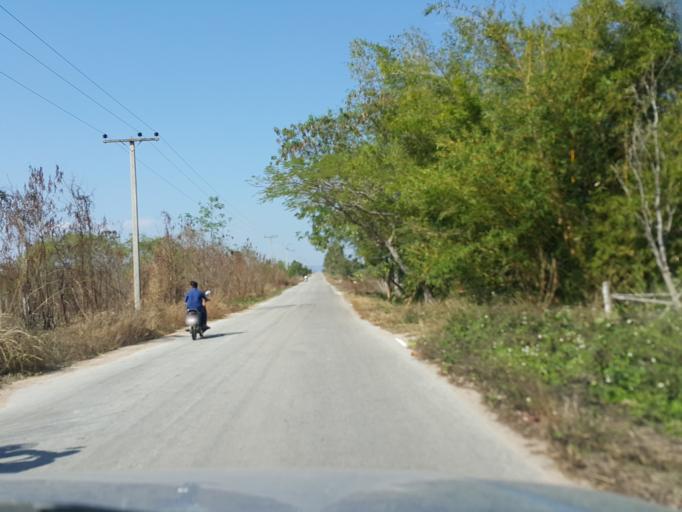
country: TH
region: Chiang Mai
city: Mae Wang
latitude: 18.5550
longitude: 98.7955
